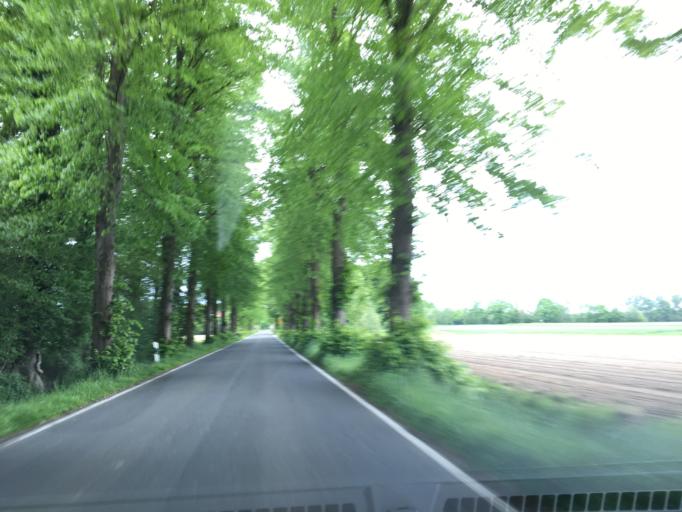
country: DE
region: North Rhine-Westphalia
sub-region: Regierungsbezirk Munster
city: Havixbeck
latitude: 51.9497
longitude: 7.5102
